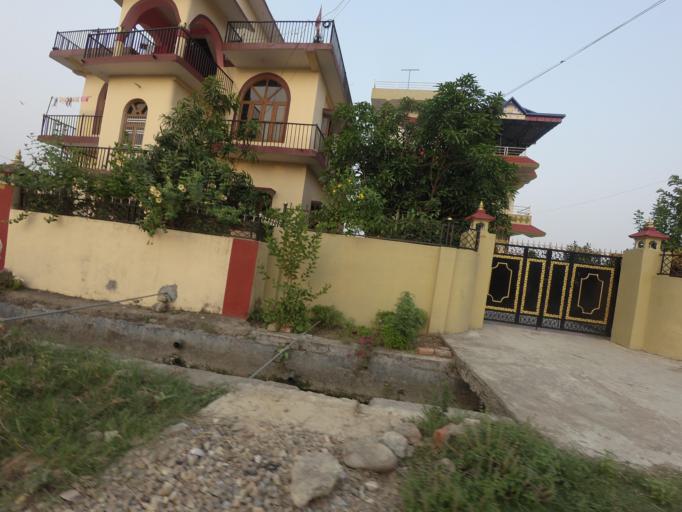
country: NP
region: Western Region
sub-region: Lumbini Zone
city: Bhairahawa
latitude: 27.5140
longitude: 83.4605
